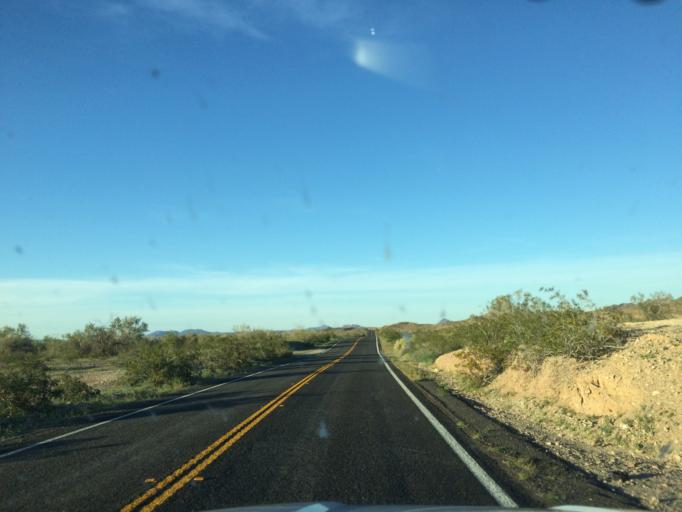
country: US
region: California
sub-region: Riverside County
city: Mesa Verde
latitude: 33.1810
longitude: -114.8652
